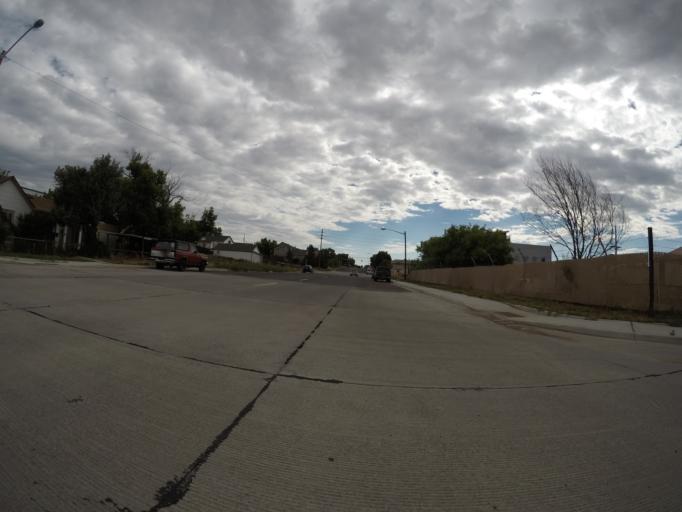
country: US
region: Wyoming
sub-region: Laramie County
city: Cheyenne
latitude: 41.1316
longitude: -104.8271
